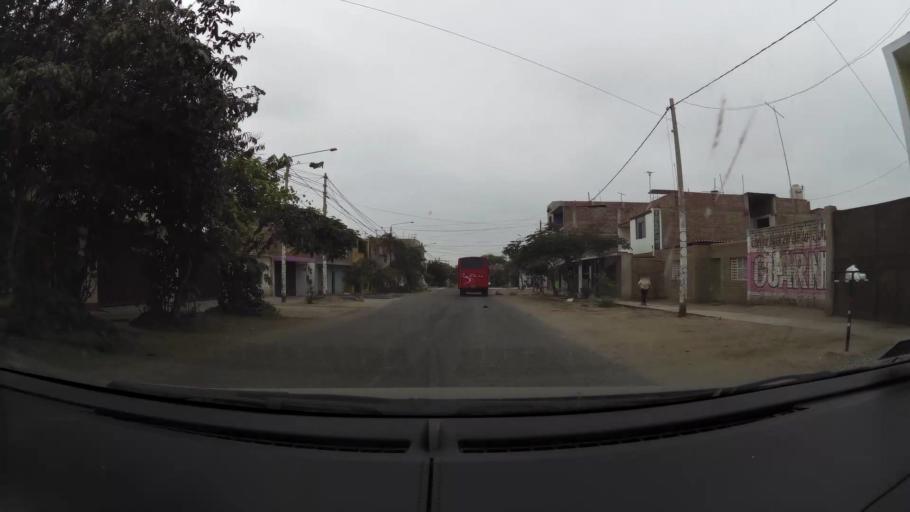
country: PE
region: La Libertad
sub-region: Provincia de Trujillo
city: La Esperanza
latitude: -8.0783
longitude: -79.0514
